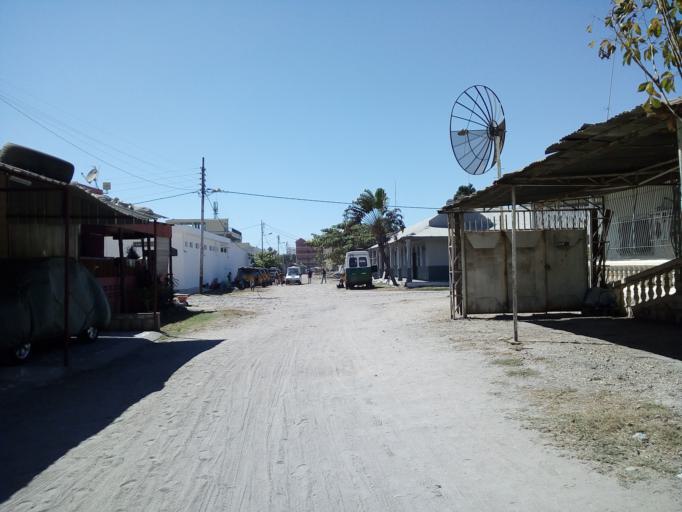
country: MG
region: Boeny
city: Mahajanga
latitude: -15.7200
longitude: 46.3156
